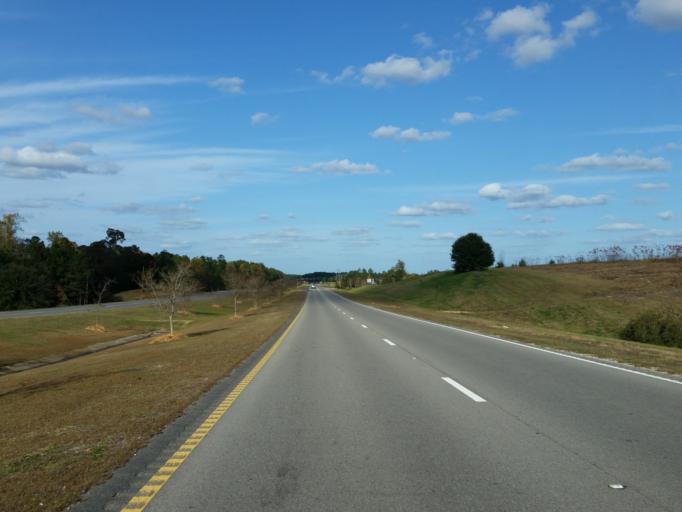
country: US
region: Mississippi
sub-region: Lamar County
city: West Hattiesburg
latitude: 31.2730
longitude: -89.3297
